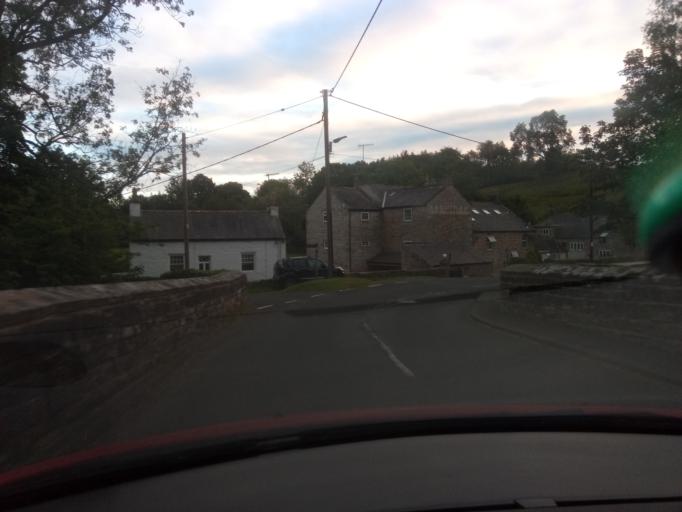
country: GB
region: England
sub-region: Northumberland
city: Bardon Mill
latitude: 54.8983
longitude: -2.2612
